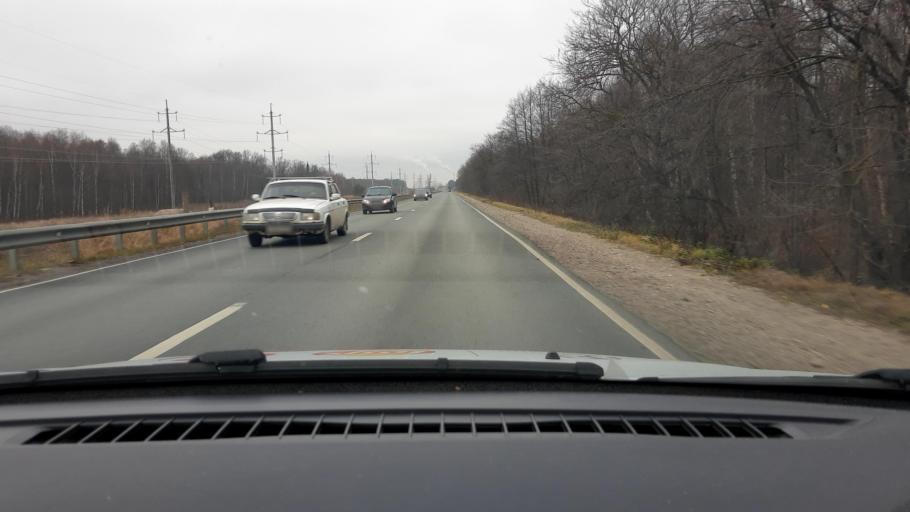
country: RU
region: Nizjnij Novgorod
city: Lukino
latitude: 56.4599
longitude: 43.6235
